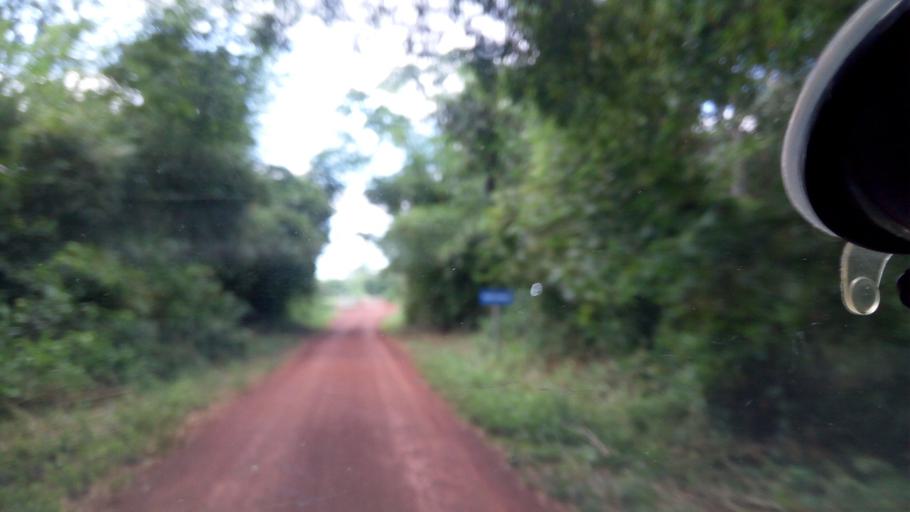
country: CD
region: Equateur
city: Libenge
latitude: 3.7961
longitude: 18.7049
